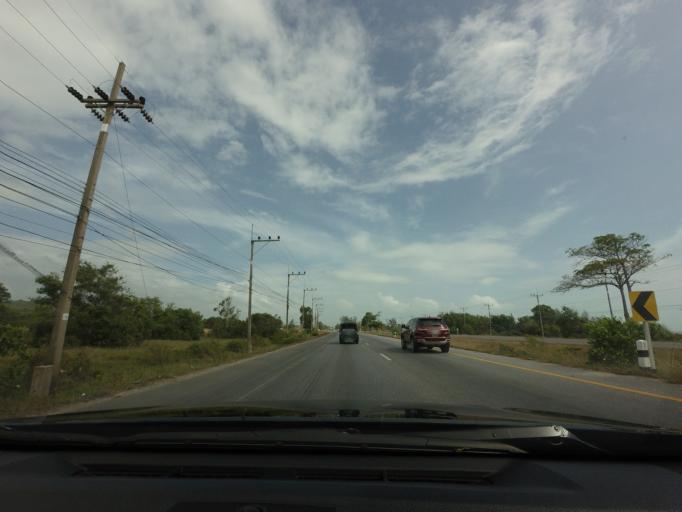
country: TH
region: Songkhla
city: Thepha
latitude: 6.9119
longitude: 100.9017
